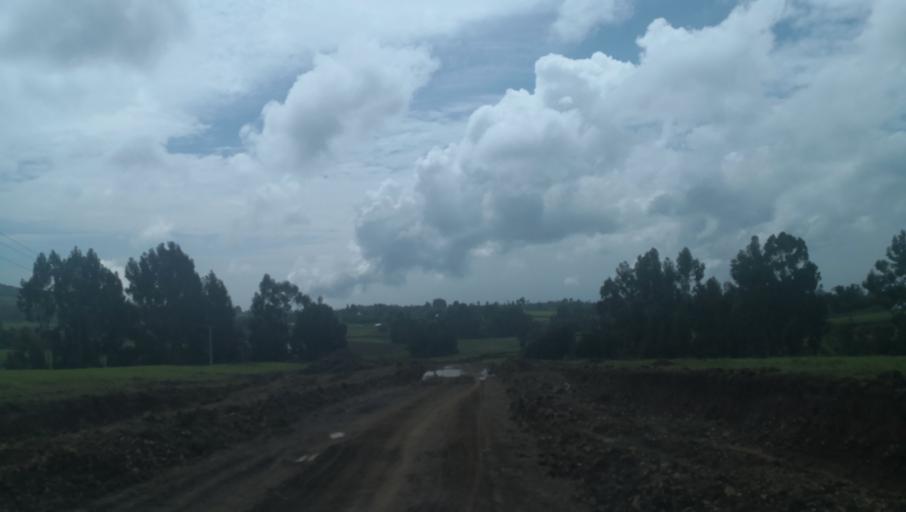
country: ET
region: Southern Nations, Nationalities, and People's Region
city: Butajira
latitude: 8.3319
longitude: 38.4049
